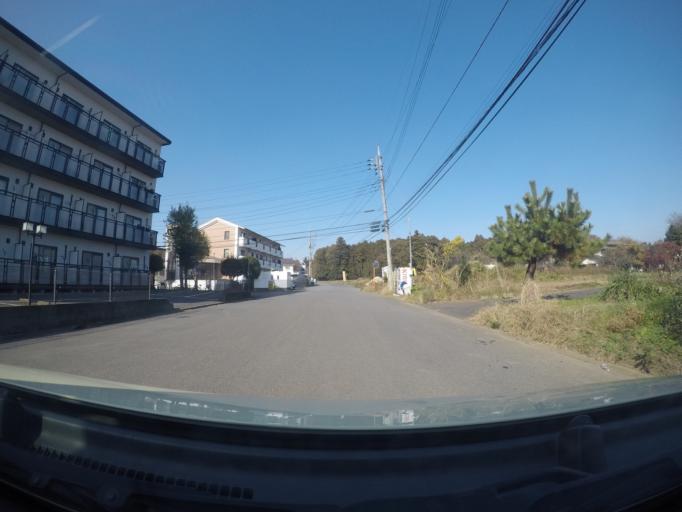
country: JP
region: Ibaraki
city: Naka
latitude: 36.0978
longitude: 140.1134
